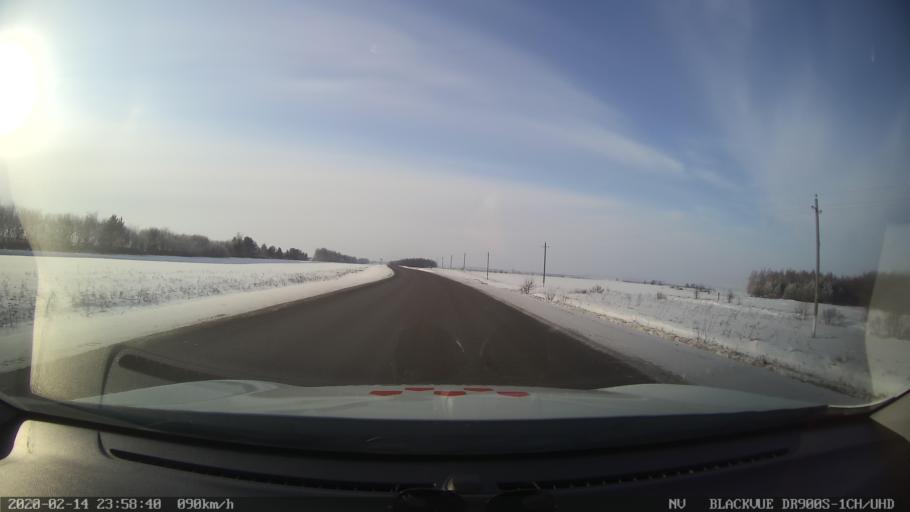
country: RU
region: Tatarstan
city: Kuybyshevskiy Zaton
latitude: 55.3419
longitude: 49.0831
